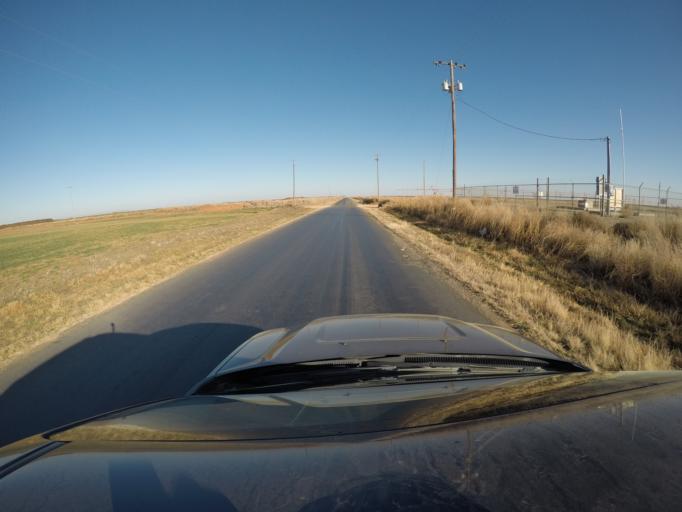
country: US
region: New Mexico
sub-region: Curry County
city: Texico
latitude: 34.3027
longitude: -103.0919
